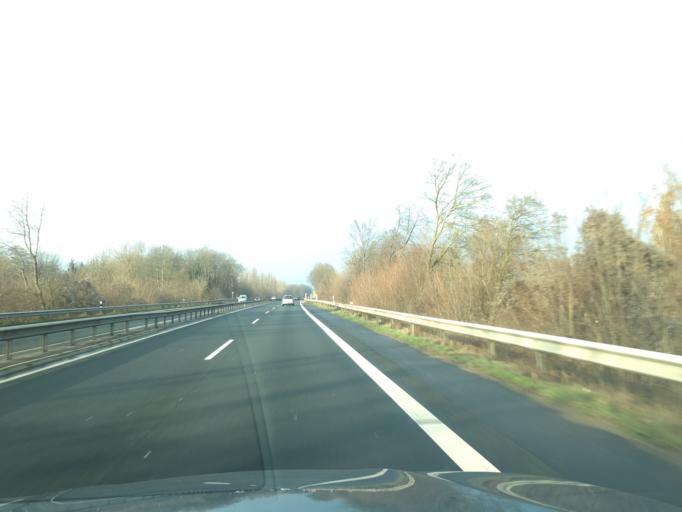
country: DE
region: Rheinland-Pfalz
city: Weissenthurm
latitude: 50.4088
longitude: 7.4492
